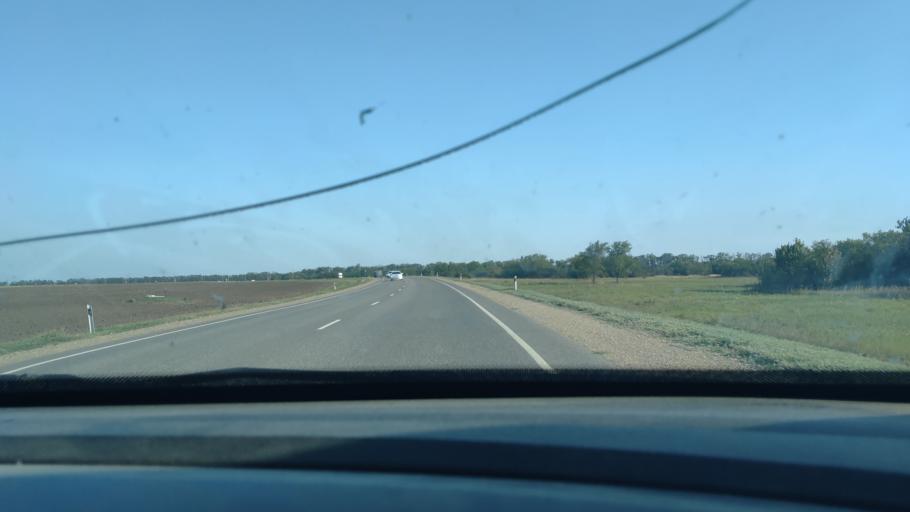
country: RU
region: Krasnodarskiy
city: Staroshcherbinovskaya
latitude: 46.6148
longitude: 38.6320
